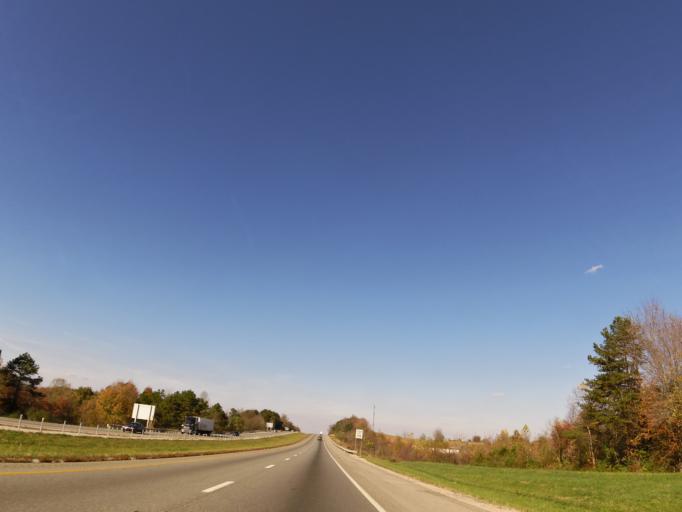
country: US
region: Kentucky
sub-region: Laurel County
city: North Corbin
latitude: 36.9864
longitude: -84.1095
